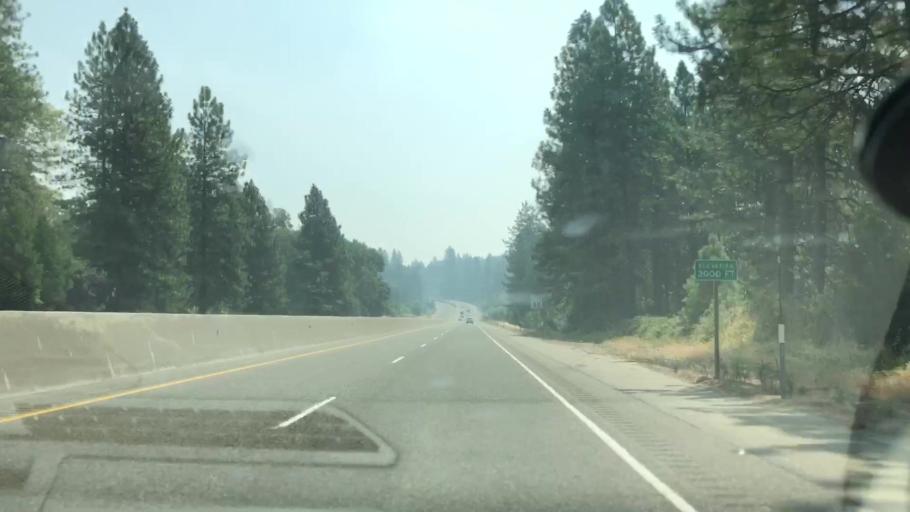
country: US
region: California
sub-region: El Dorado County
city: Camino
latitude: 38.7377
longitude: -120.6894
